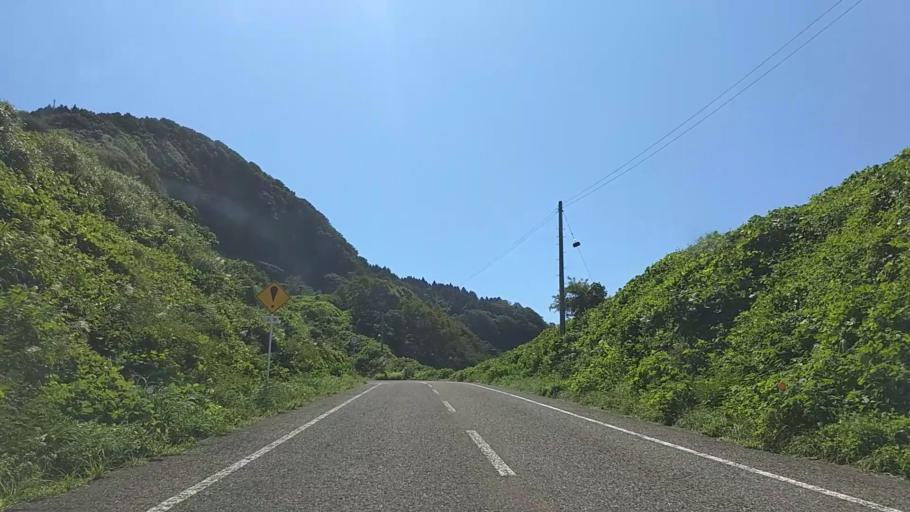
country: JP
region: Niigata
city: Joetsu
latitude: 37.1703
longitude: 138.0947
